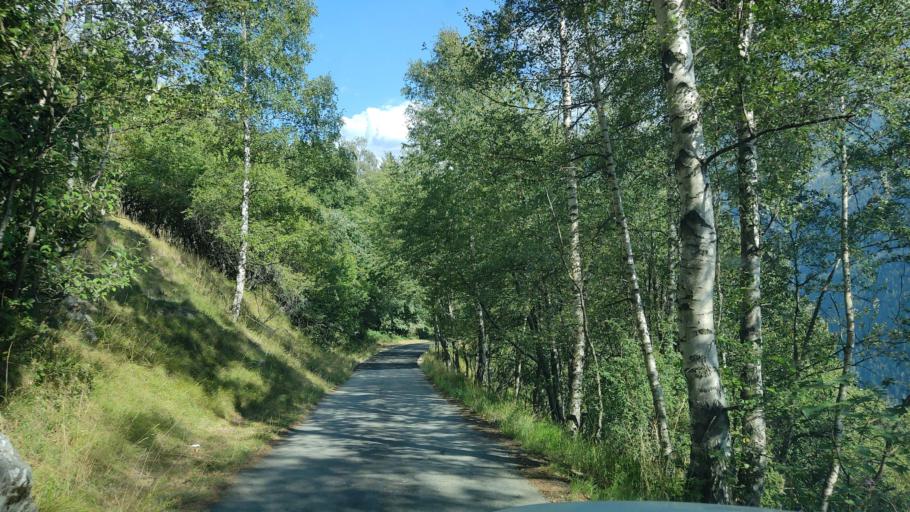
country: FR
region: Rhone-Alpes
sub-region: Departement de la Savoie
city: Val Thorens
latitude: 45.2182
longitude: 6.5576
